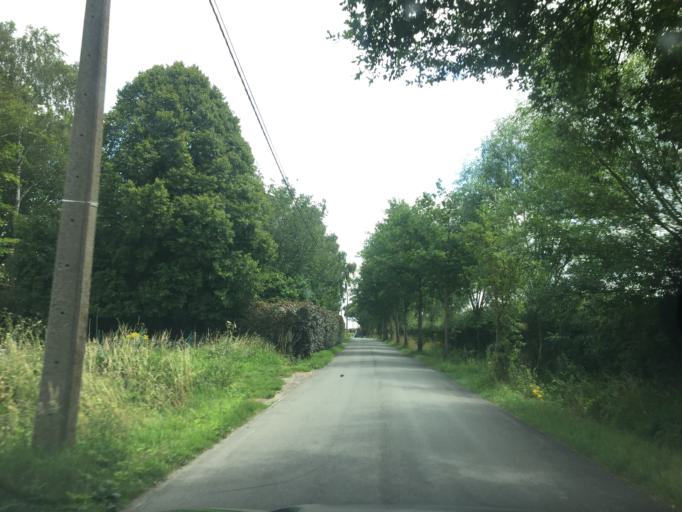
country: BE
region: Flanders
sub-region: Provincie West-Vlaanderen
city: Torhout
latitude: 51.0507
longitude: 3.1195
